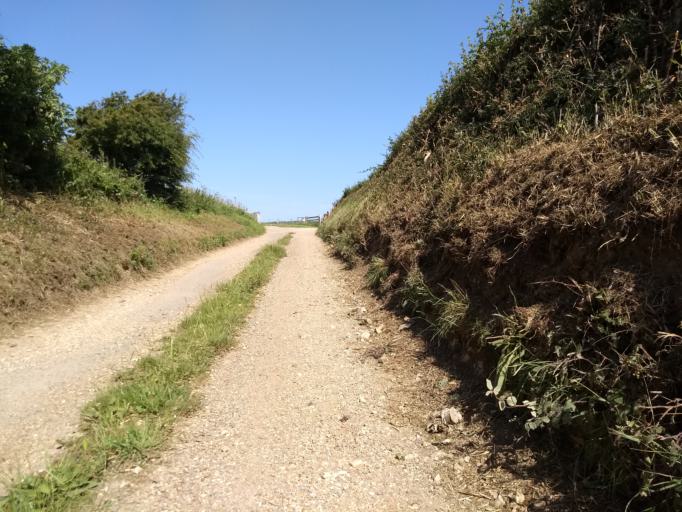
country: GB
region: England
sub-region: Isle of Wight
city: Chale
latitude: 50.6528
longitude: -1.3577
